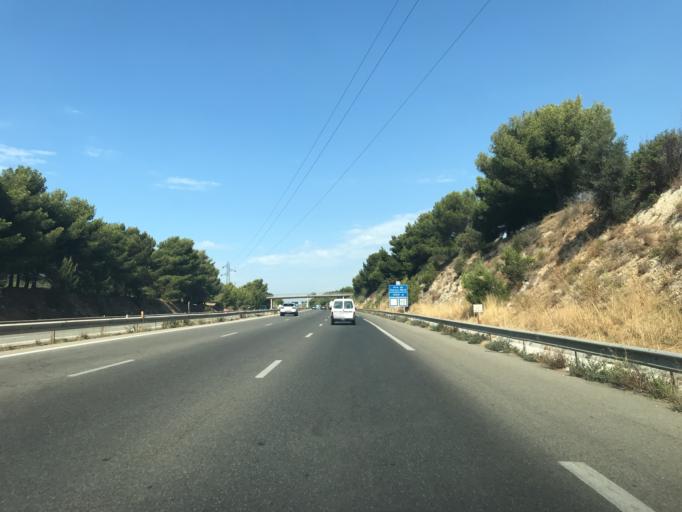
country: FR
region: Provence-Alpes-Cote d'Azur
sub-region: Departement du Var
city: Sanary-sur-Mer
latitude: 43.1383
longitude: 5.8027
